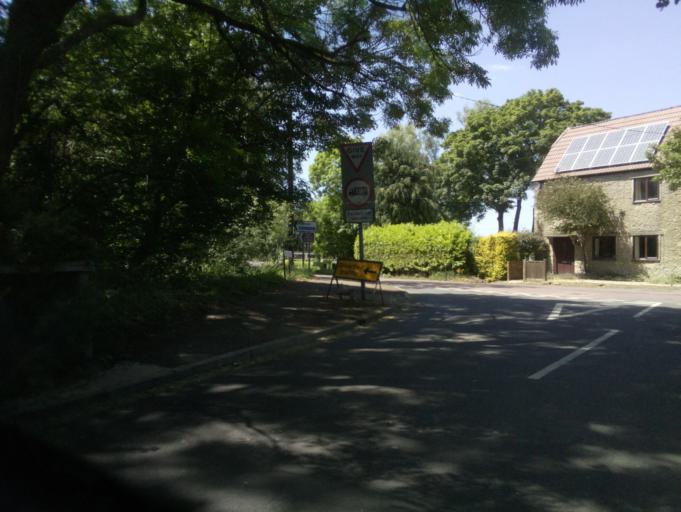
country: GB
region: England
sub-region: Wiltshire
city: Bremhill
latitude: 51.5114
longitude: -2.0573
